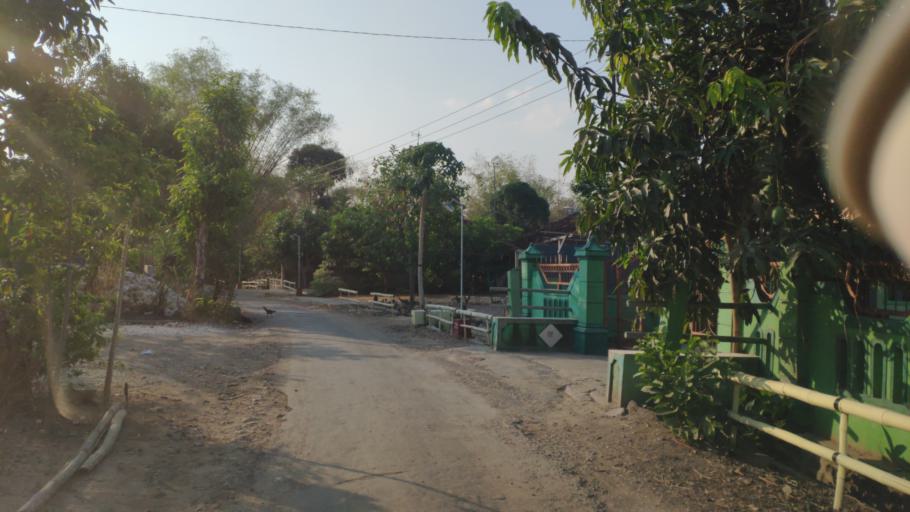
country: ID
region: Central Java
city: Cangkringan
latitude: -6.9769
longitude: 111.4630
